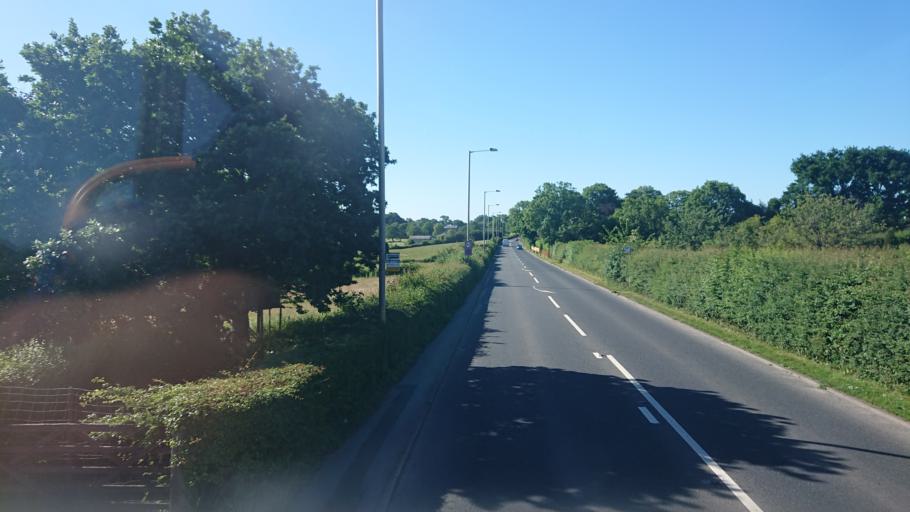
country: GB
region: England
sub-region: Lancashire
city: Bay Horse
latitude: 53.9620
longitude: -2.7763
